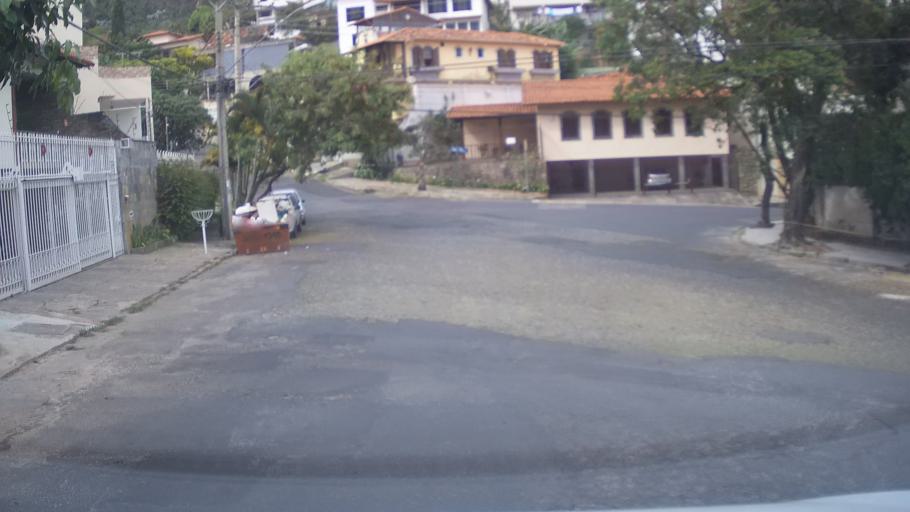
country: BR
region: Minas Gerais
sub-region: Belo Horizonte
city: Belo Horizonte
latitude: -19.9539
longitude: -43.9206
